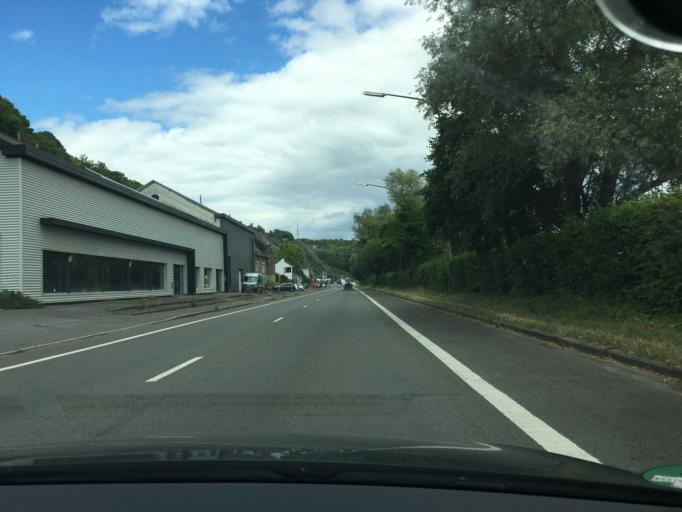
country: BE
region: Wallonia
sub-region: Province de Liege
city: Huy
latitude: 50.5352
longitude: 5.2506
